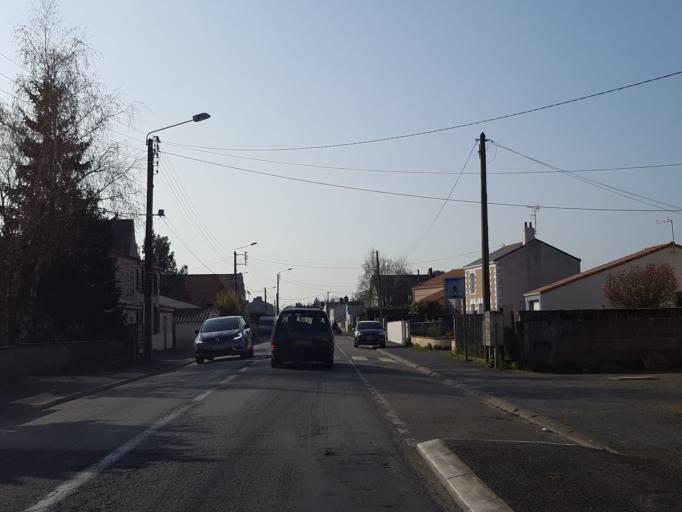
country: FR
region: Pays de la Loire
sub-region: Departement de la Loire-Atlantique
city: Geneston
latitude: 47.0591
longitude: -1.5146
